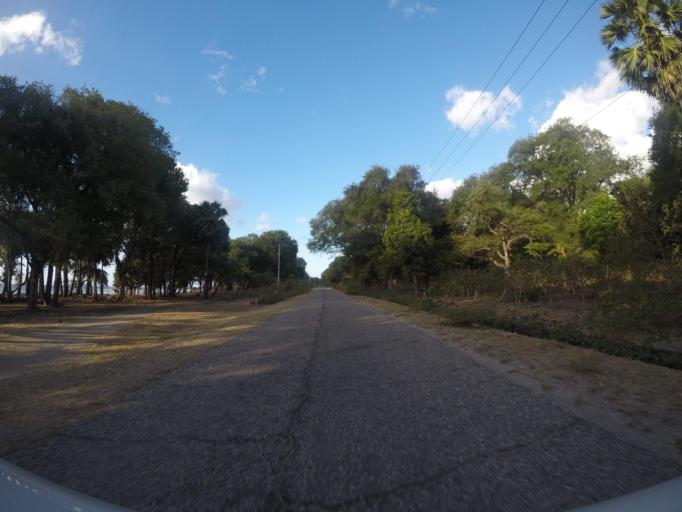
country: TL
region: Lautem
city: Lospalos
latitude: -8.3465
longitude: 126.9252
